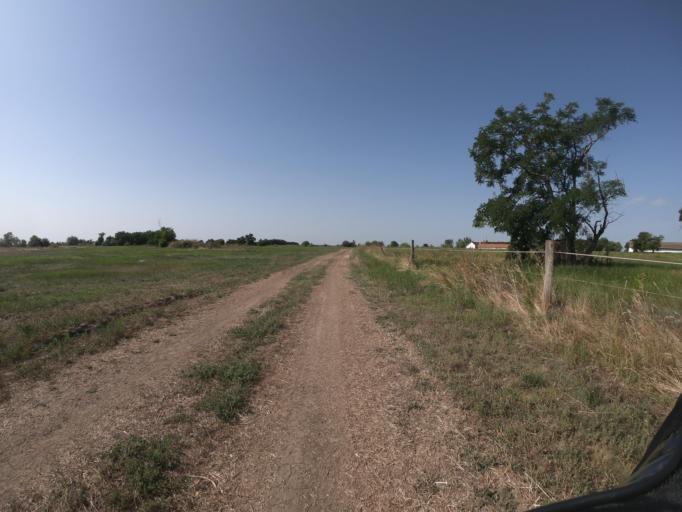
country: HU
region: Hajdu-Bihar
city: Egyek
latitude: 47.5733
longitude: 20.9462
